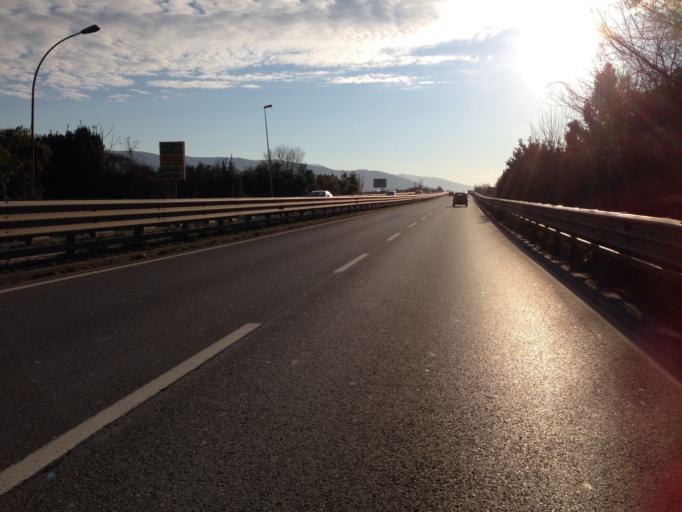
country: IT
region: Tuscany
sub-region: Provincia di Prato
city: Fornacelle
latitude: 43.8827
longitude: 11.0458
